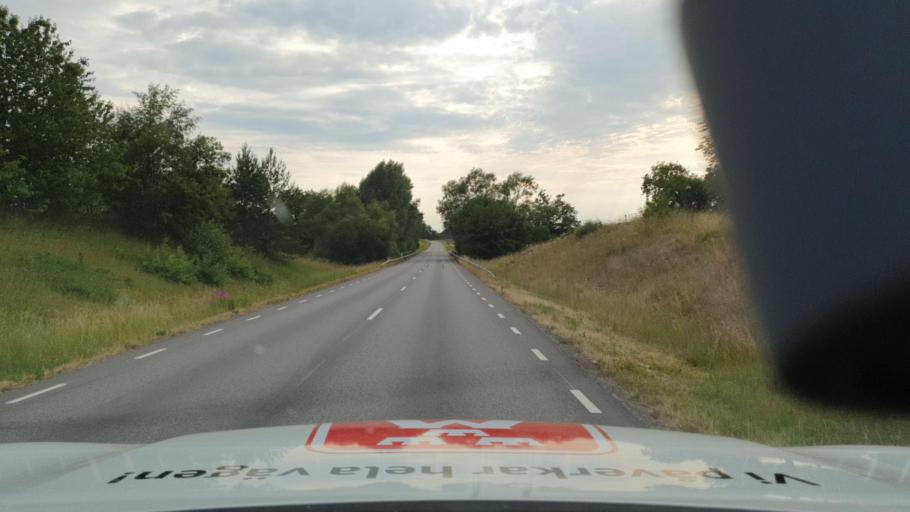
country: SE
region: Skane
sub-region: Sjobo Kommun
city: Sjoebo
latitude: 55.6381
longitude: 13.7617
